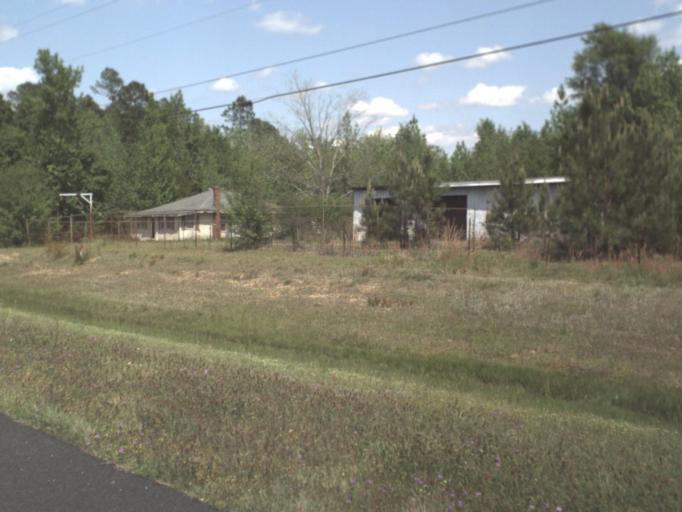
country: US
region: Florida
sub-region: Escambia County
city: Century
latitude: 30.9473
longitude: -87.2858
